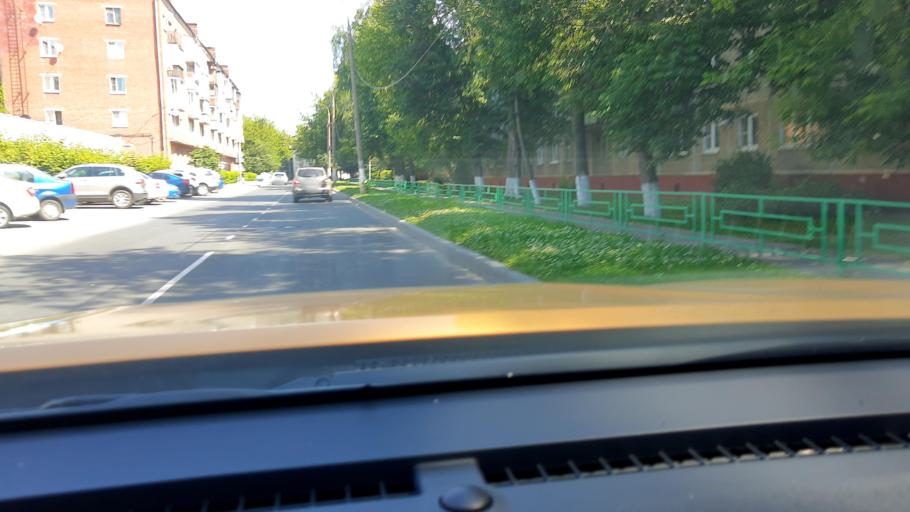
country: RU
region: Moskovskaya
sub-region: Podol'skiy Rayon
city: Podol'sk
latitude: 55.4289
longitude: 37.5577
